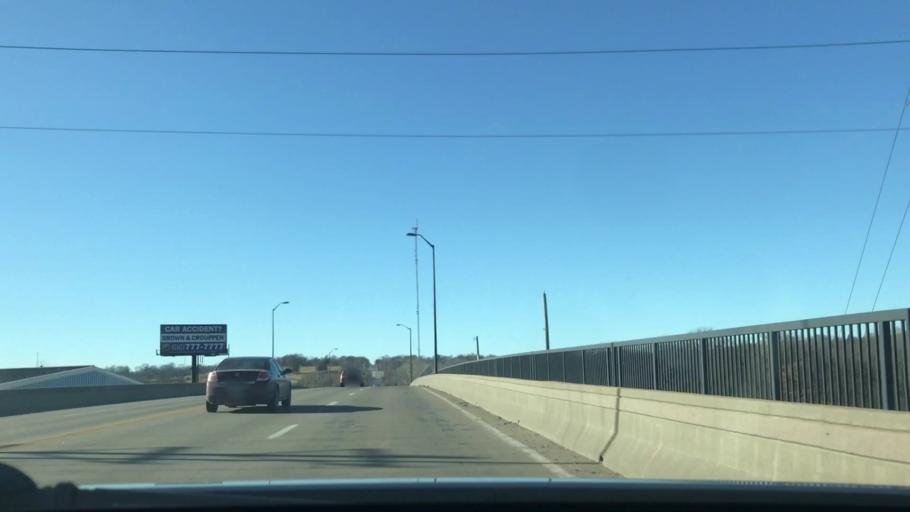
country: US
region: Missouri
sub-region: Jackson County
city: Sugar Creek
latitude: 39.0826
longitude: -94.4928
